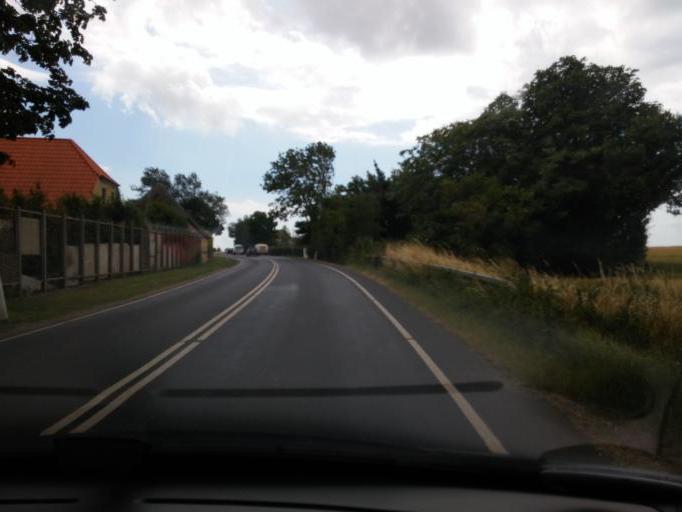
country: DK
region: South Denmark
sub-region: Langeland Kommune
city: Rudkobing
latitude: 54.9139
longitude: 10.7311
